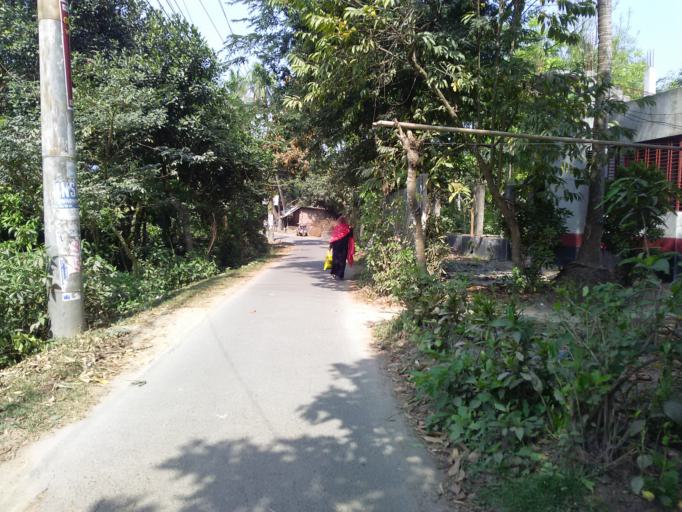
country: BD
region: Khulna
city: Khulna
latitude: 22.8783
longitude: 89.5409
